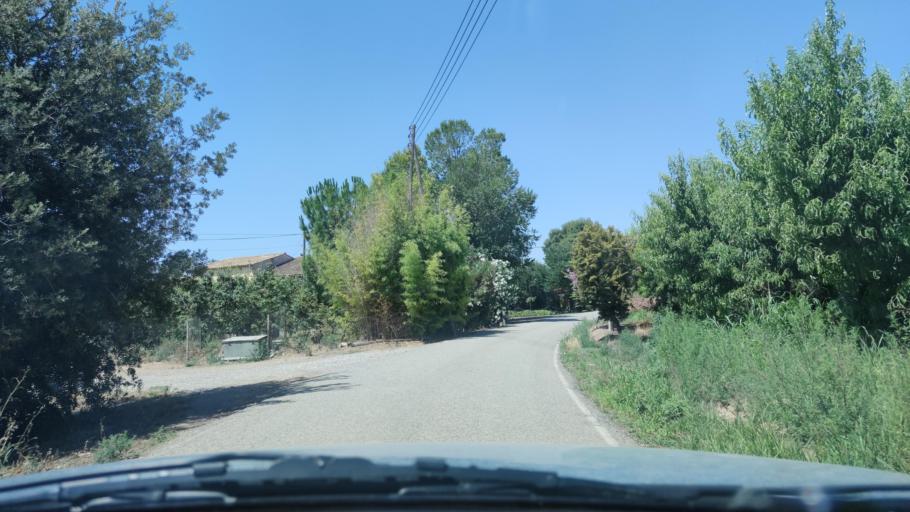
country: ES
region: Catalonia
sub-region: Provincia de Lleida
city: Torrefarrera
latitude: 41.6475
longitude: 0.5993
